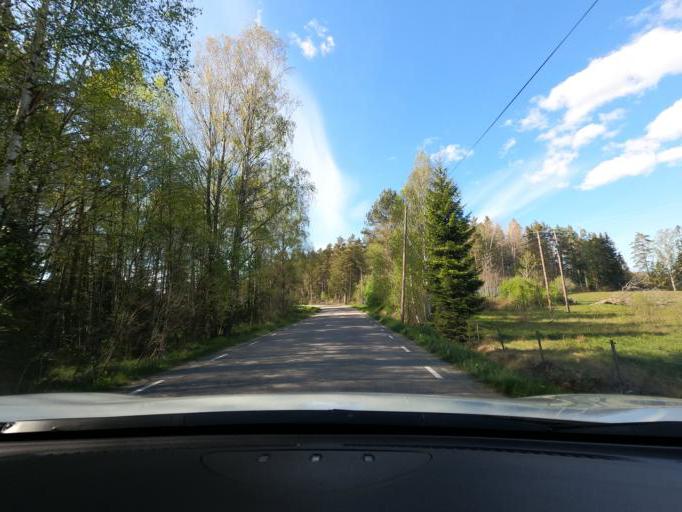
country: SE
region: Vaestra Goetaland
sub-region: Harryda Kommun
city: Ravlanda
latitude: 57.6455
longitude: 12.4975
